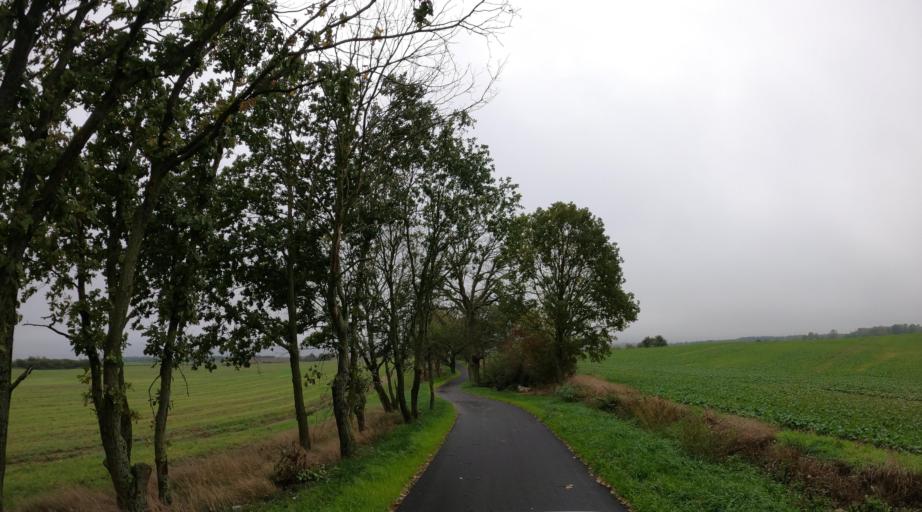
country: PL
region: West Pomeranian Voivodeship
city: Trzcinsko Zdroj
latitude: 52.9300
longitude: 14.7273
